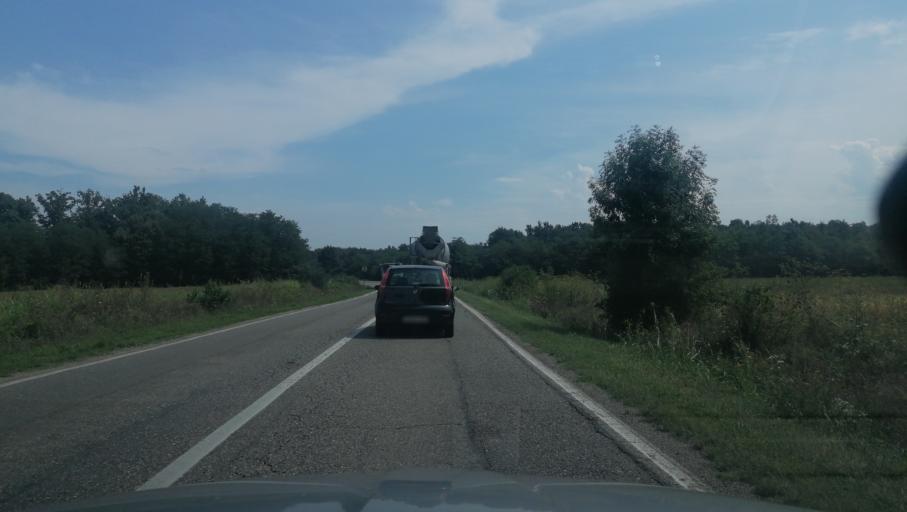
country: BA
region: Republika Srpska
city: Velika Obarska
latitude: 44.7754
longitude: 19.1124
